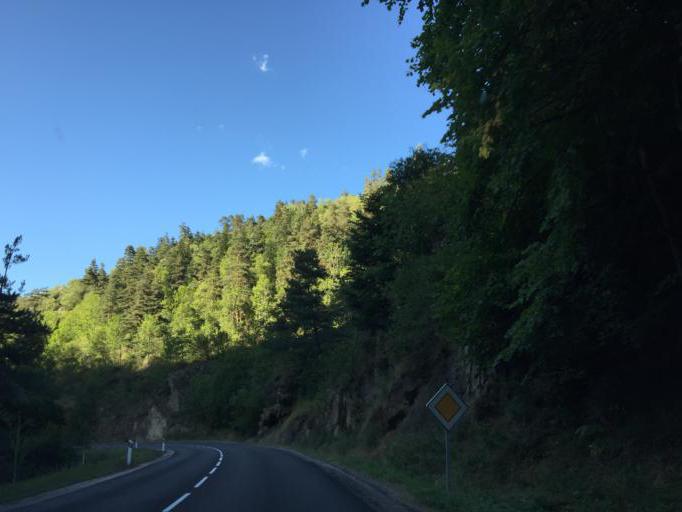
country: FR
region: Auvergne
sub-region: Departement de la Haute-Loire
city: Saugues
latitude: 44.9562
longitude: 3.6304
